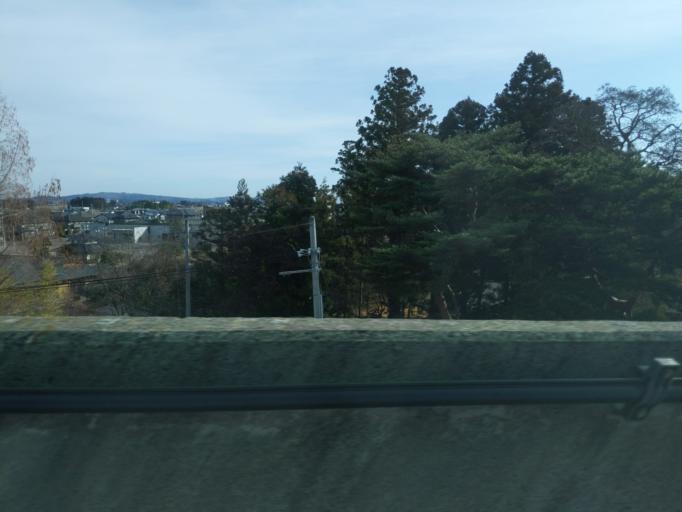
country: JP
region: Miyagi
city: Furukawa
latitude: 38.5818
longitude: 140.9708
